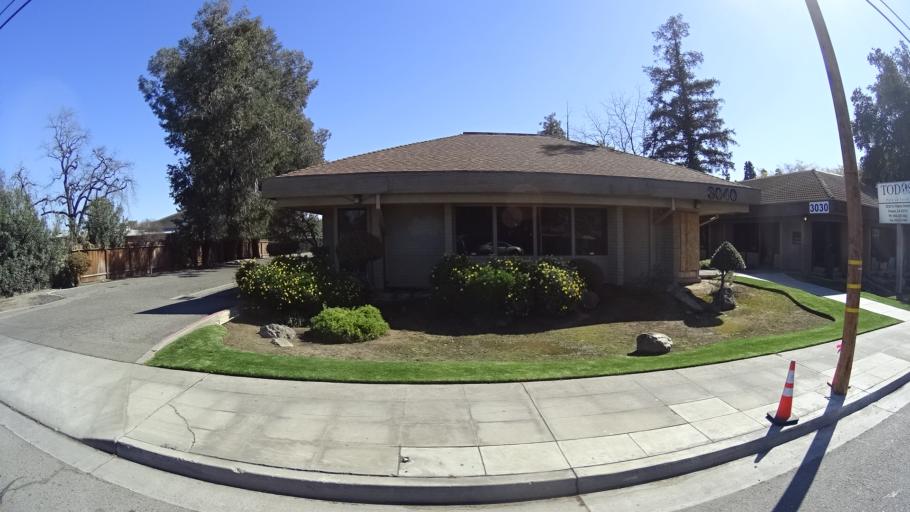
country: US
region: California
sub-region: Fresno County
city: Fresno
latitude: 36.7784
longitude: -119.7815
